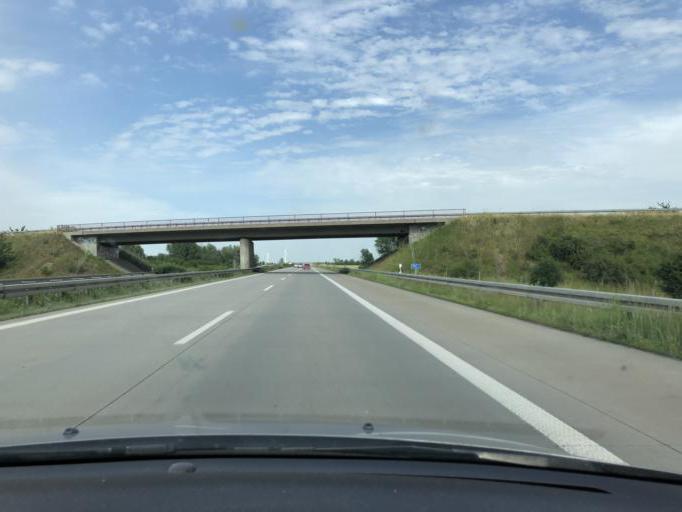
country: DE
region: Saxony
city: Kitzen
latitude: 51.2478
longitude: 12.2277
